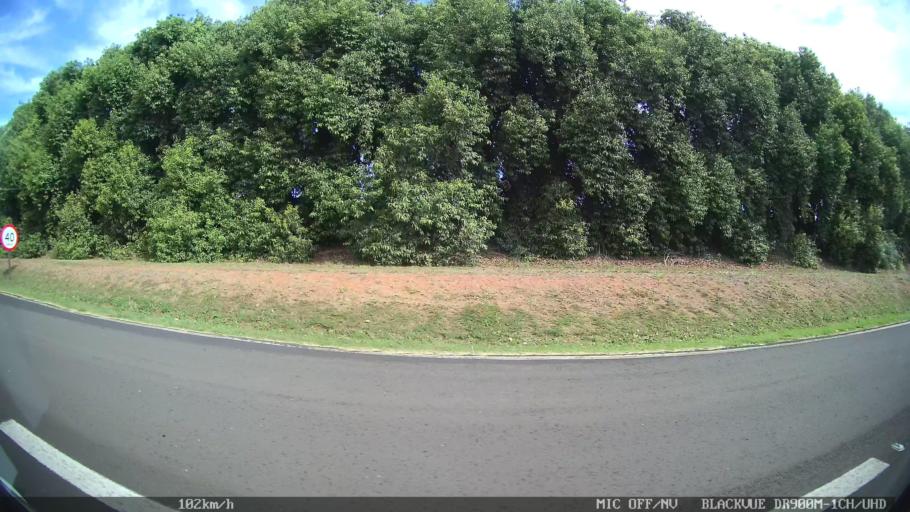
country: BR
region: Sao Paulo
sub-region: Matao
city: Matao
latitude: -21.6356
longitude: -48.3996
